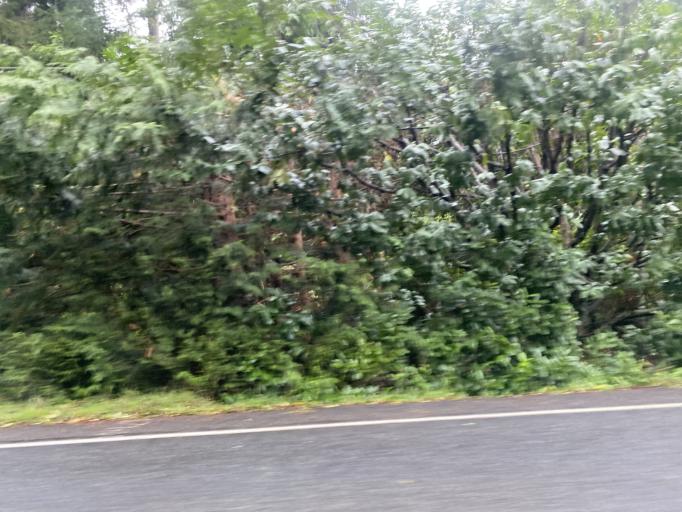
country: US
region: Washington
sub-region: Island County
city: Camano
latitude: 48.0954
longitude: -122.5189
